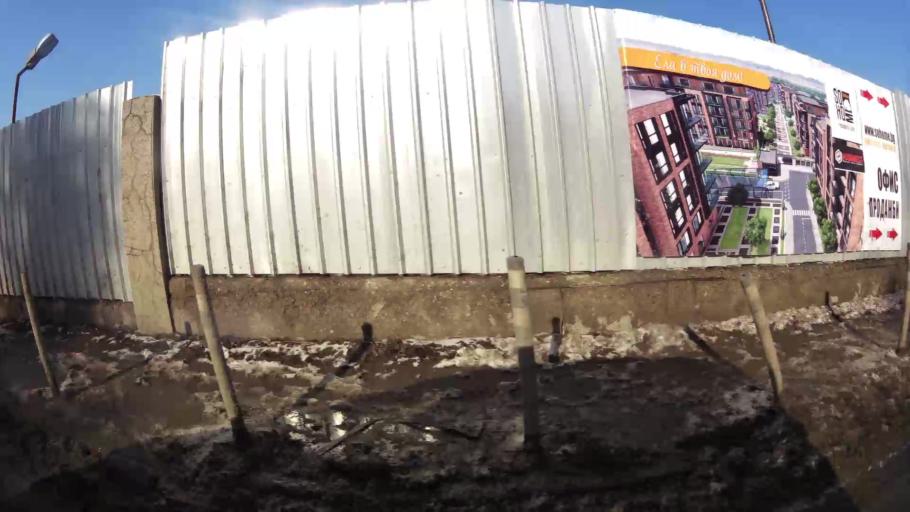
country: BG
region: Sofia-Capital
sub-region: Stolichna Obshtina
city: Sofia
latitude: 42.6593
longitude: 23.3266
